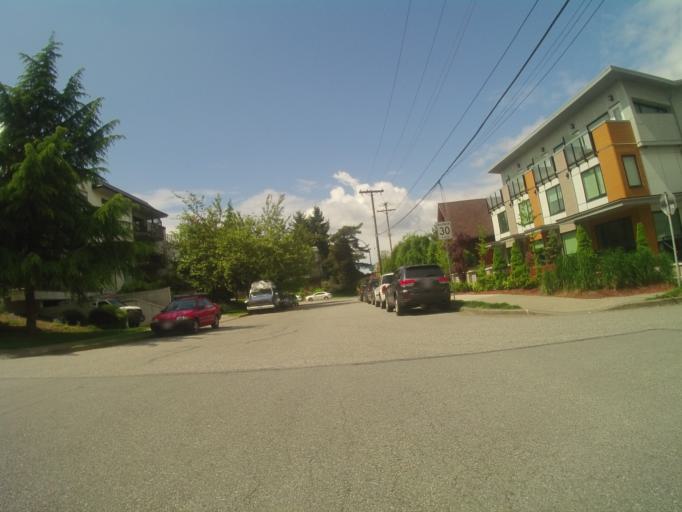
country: CA
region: British Columbia
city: Vancouver
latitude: 49.2653
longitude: -123.0948
